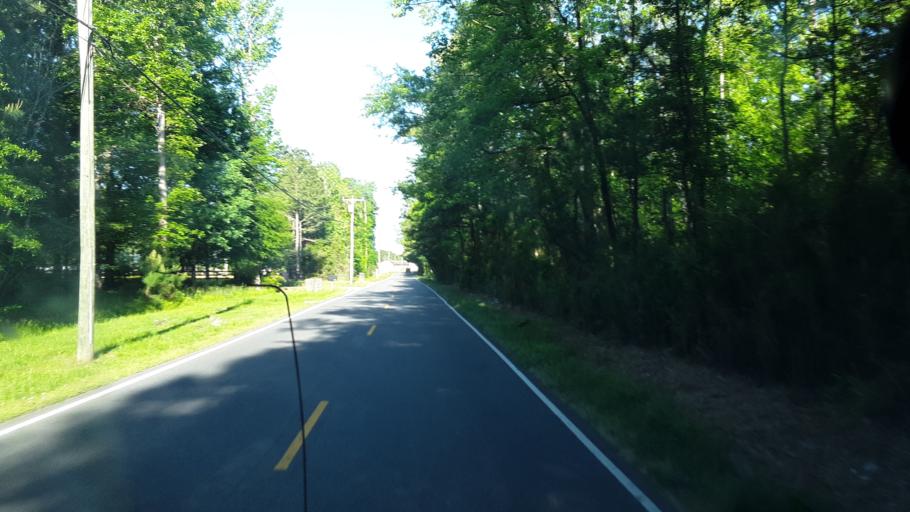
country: US
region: Virginia
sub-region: City of Virginia Beach
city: Virginia Beach
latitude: 36.7205
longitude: -76.0405
